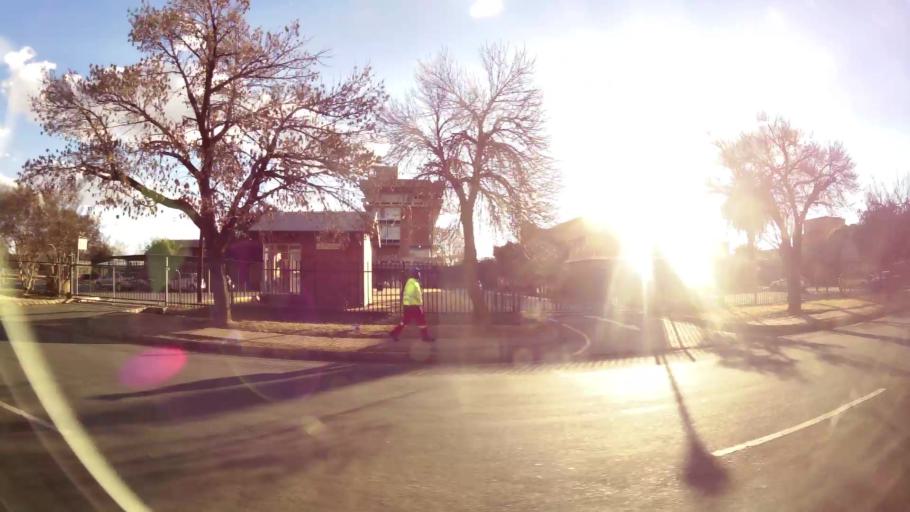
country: ZA
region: North-West
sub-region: Dr Kenneth Kaunda District Municipality
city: Potchefstroom
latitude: -26.7307
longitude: 27.0841
